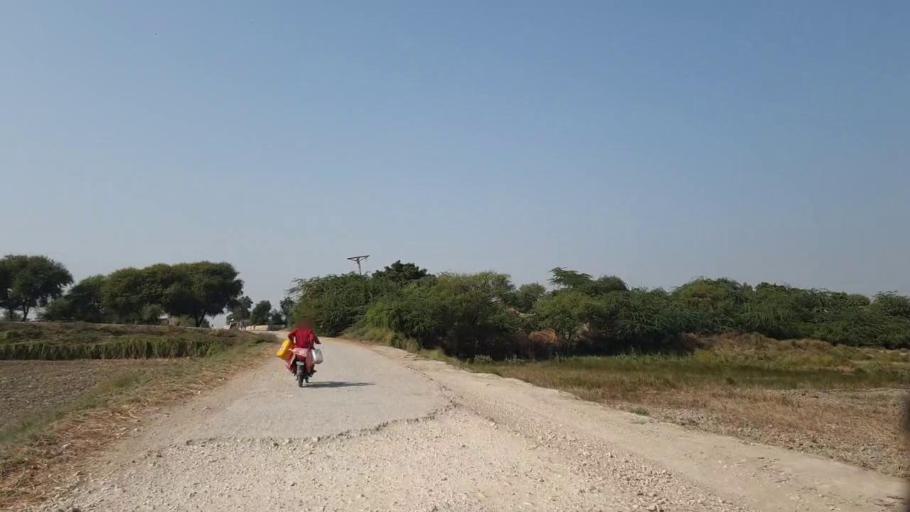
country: PK
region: Sindh
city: Bulri
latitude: 24.9600
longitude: 68.3296
